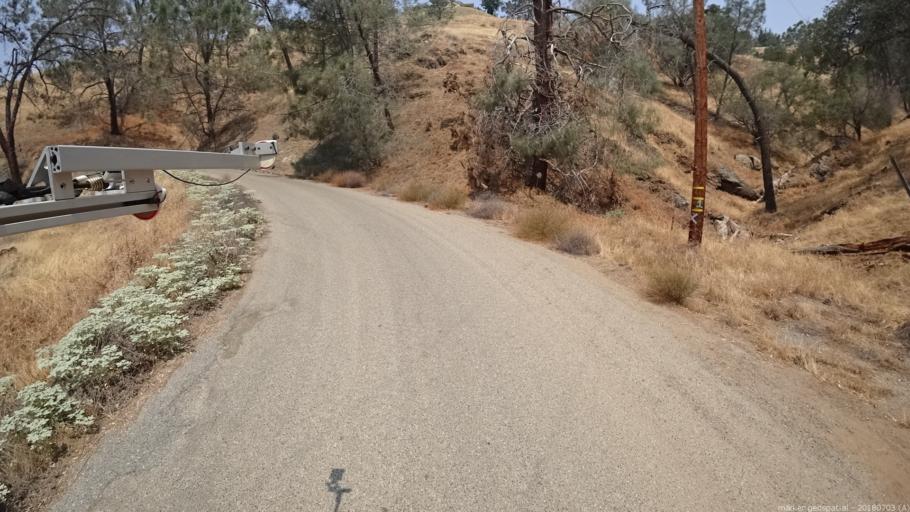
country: US
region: California
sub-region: Fresno County
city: Auberry
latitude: 37.0511
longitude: -119.6503
